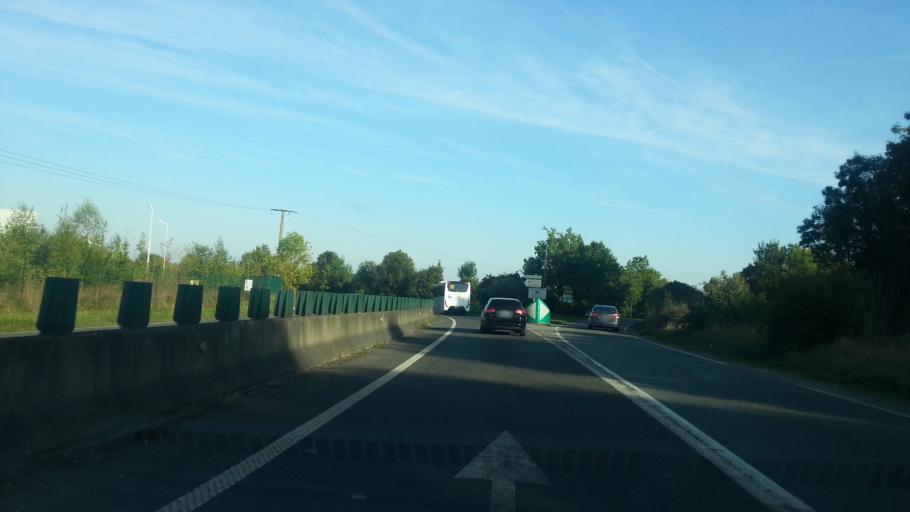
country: FR
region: Picardie
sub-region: Departement de l'Oise
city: Beauvais
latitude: 49.4563
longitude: 2.0694
